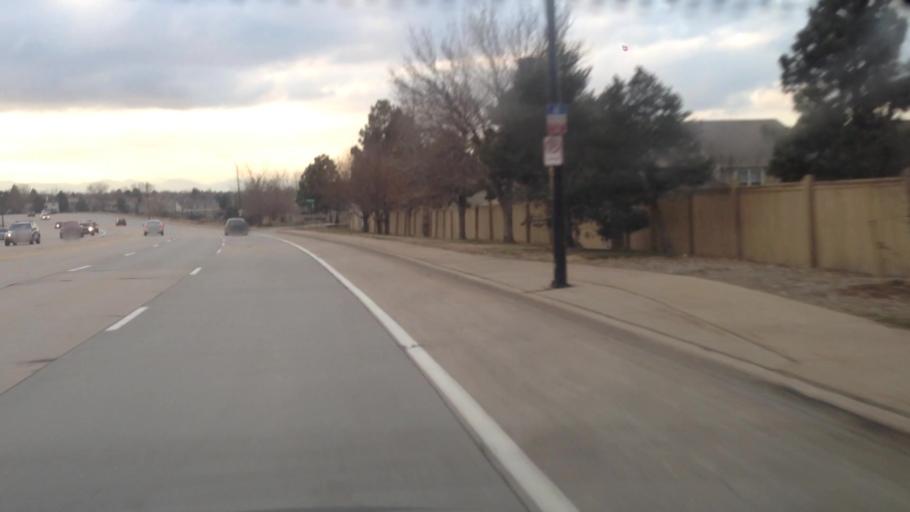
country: US
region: Colorado
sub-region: Douglas County
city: Carriage Club
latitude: 39.5440
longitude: -104.9169
